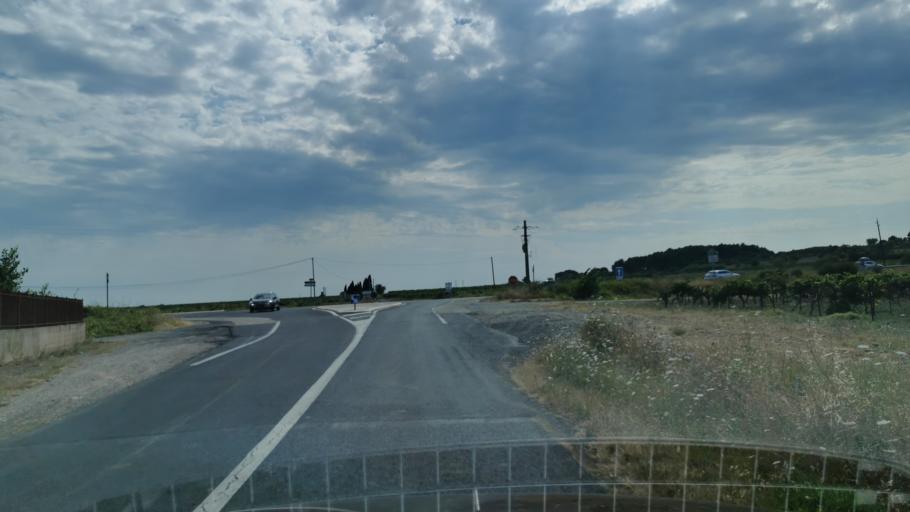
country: FR
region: Languedoc-Roussillon
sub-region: Departement de l'Herault
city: Cazouls-les-Beziers
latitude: 43.3651
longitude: 3.0882
